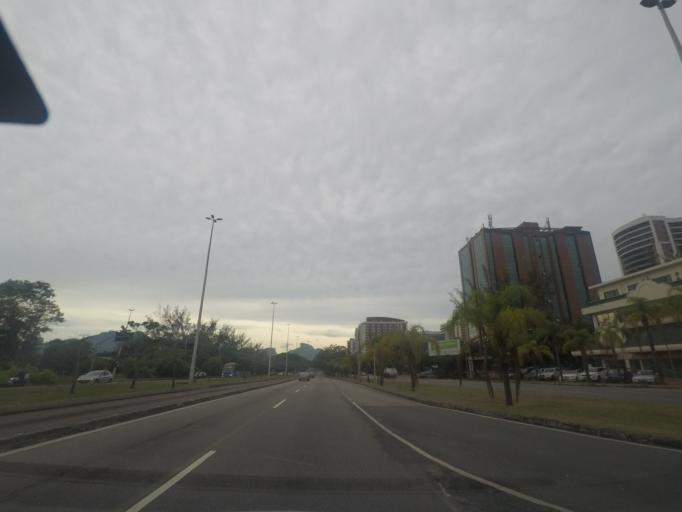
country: BR
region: Rio de Janeiro
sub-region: Nilopolis
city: Nilopolis
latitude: -23.0004
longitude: -43.3954
